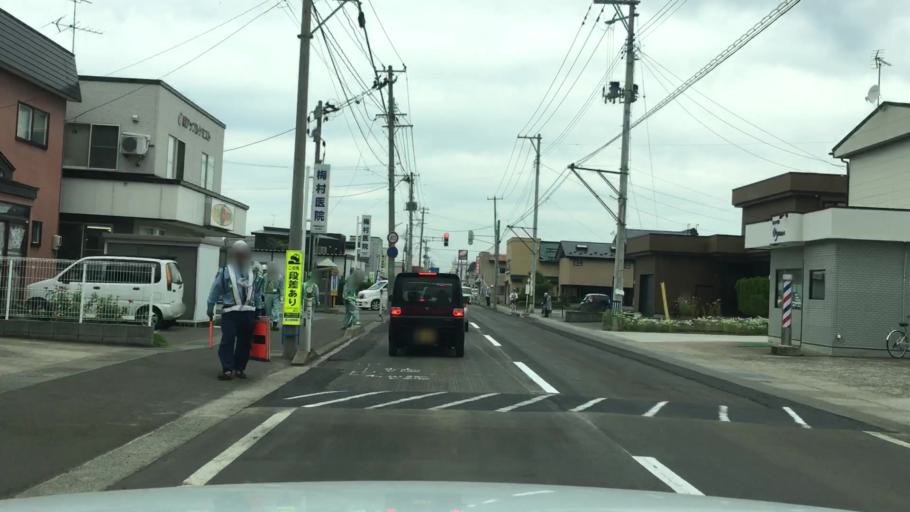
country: JP
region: Aomori
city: Hirosaki
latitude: 40.6263
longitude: 140.4552
